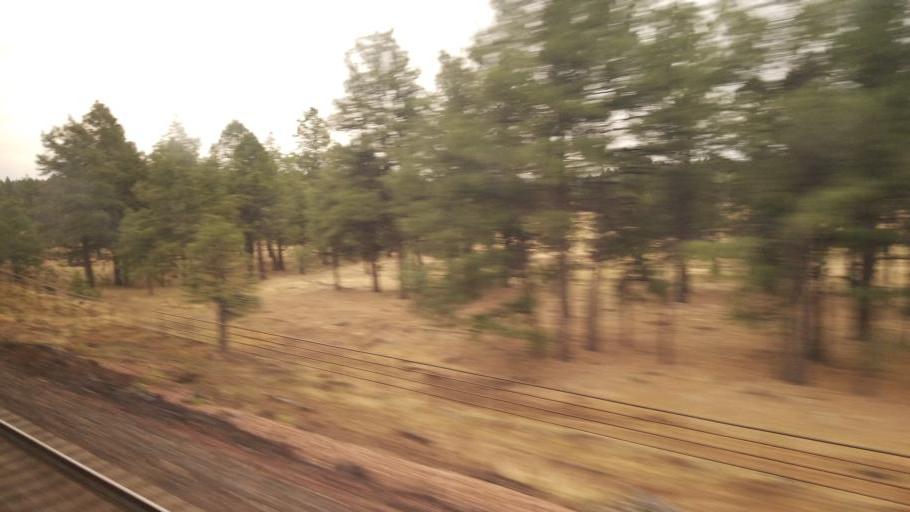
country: US
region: Arizona
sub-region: Coconino County
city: Parks
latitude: 35.2351
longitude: -112.0038
